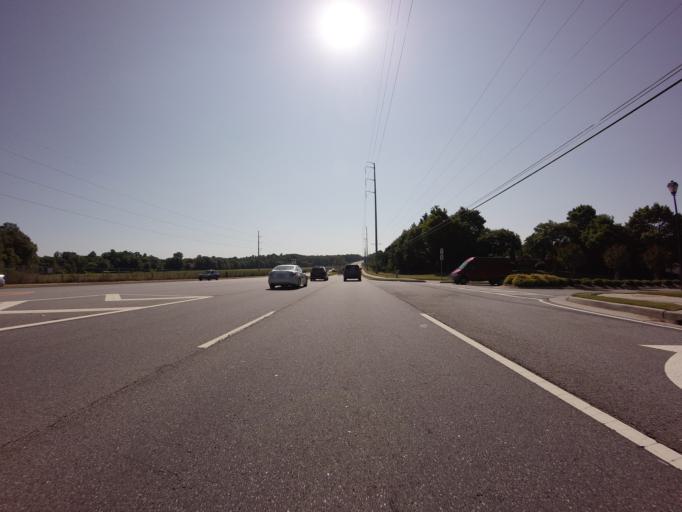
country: US
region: Georgia
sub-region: Gwinnett County
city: Suwanee
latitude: 34.0508
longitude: -84.1082
